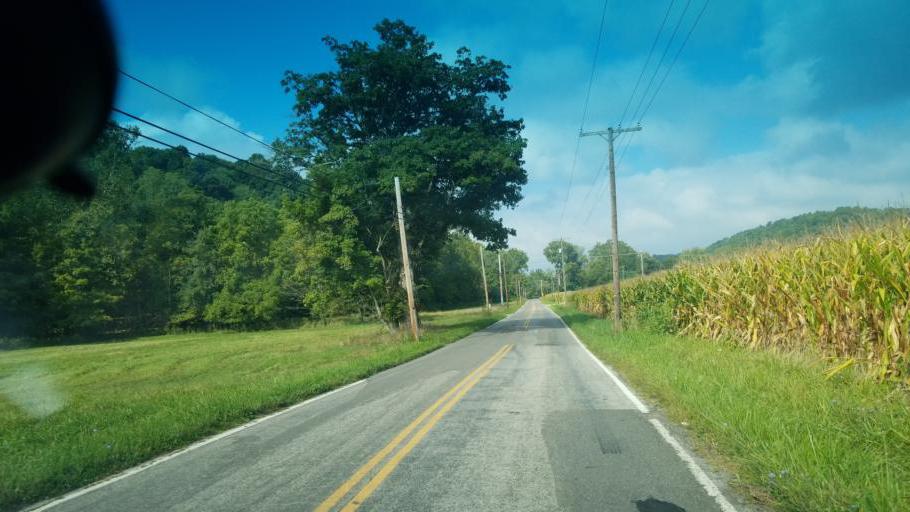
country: US
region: Ohio
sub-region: Licking County
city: Granville
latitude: 40.1196
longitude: -82.4677
